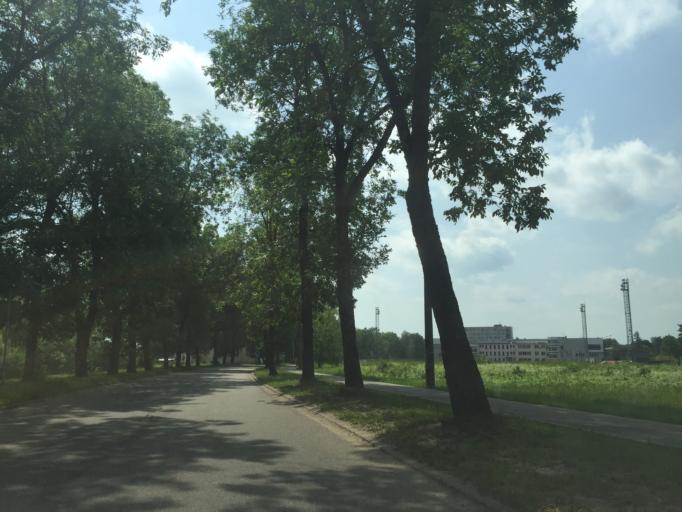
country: LV
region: Olaine
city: Olaine
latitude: 56.7905
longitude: 23.9461
